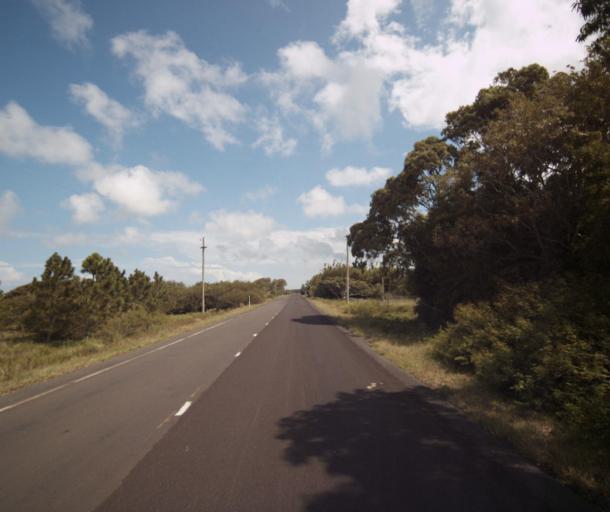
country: BR
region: Rio Grande do Sul
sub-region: Tapes
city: Tapes
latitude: -31.4036
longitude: -51.1652
